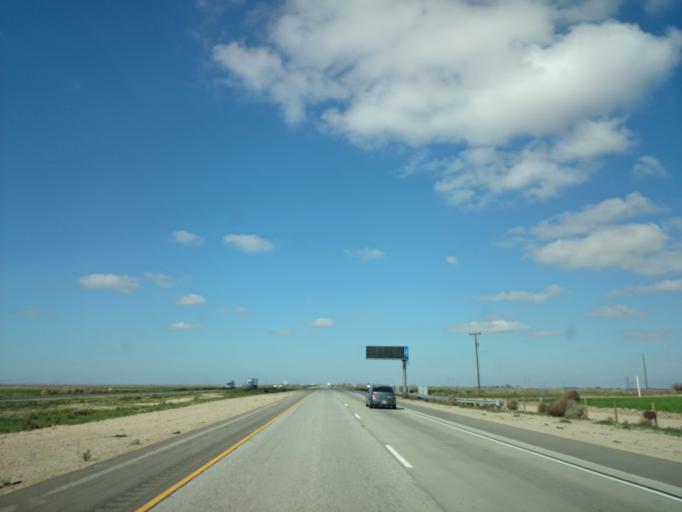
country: US
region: California
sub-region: Kern County
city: Buttonwillow
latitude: 35.3647
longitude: -119.3495
